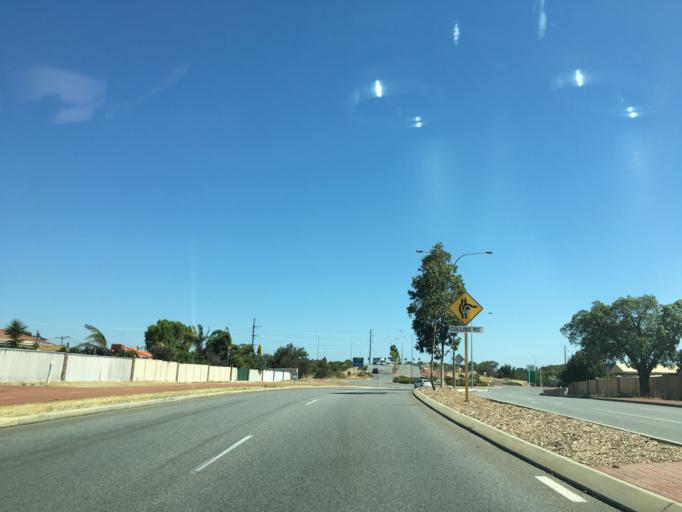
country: AU
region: Western Australia
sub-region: Canning
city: Canning Vale
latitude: -32.0539
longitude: 115.9045
